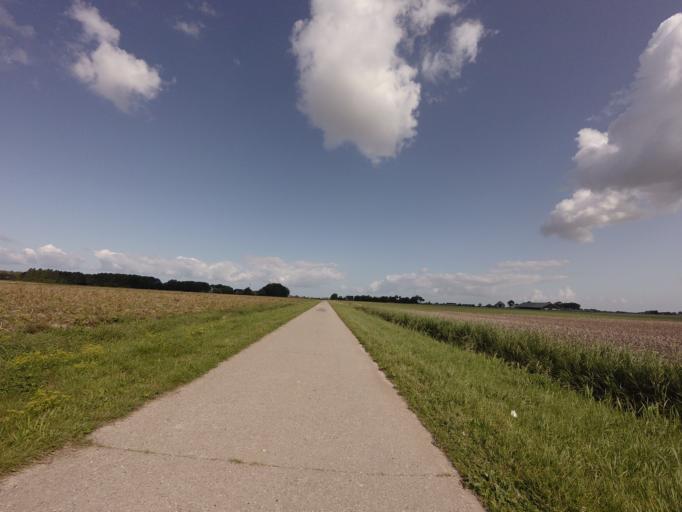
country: NL
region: Friesland
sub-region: Gemeente Het Bildt
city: Sint Jacobiparochie
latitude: 53.2682
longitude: 5.6163
